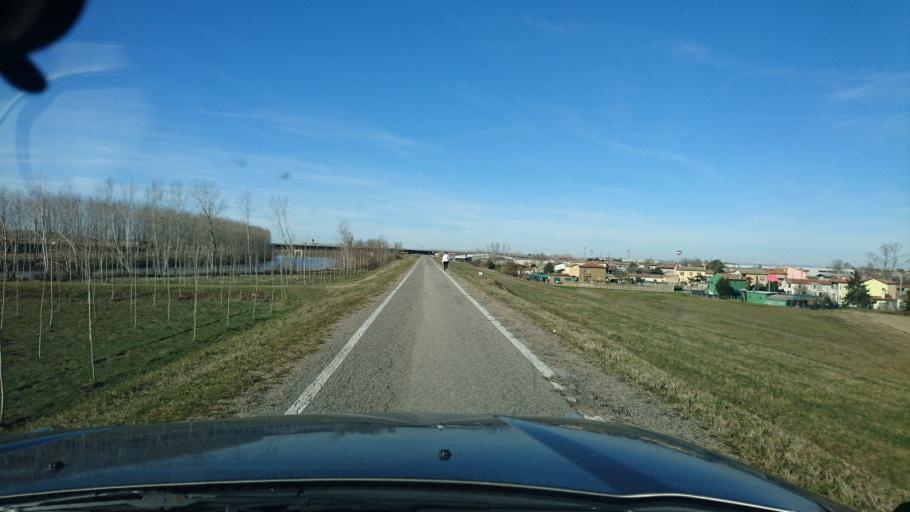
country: IT
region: Veneto
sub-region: Provincia di Rovigo
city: Ariano
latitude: 44.9370
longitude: 12.1296
